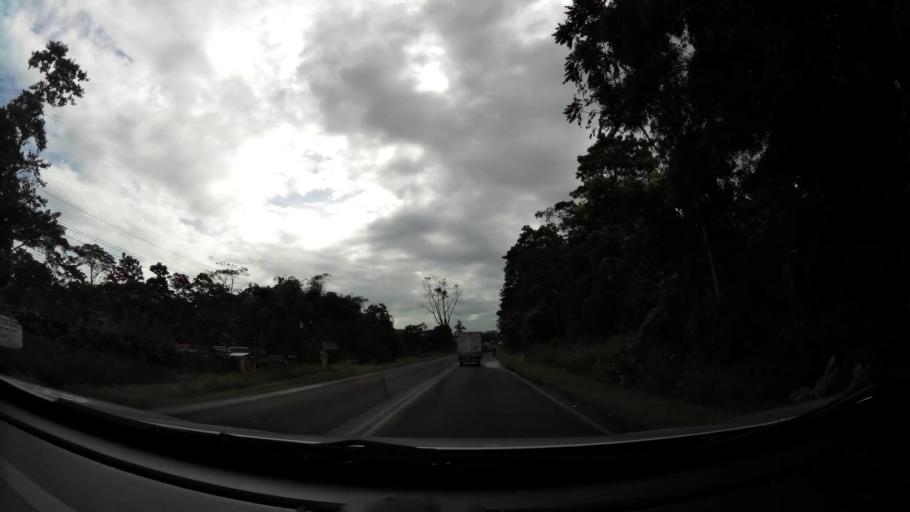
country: CR
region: Limon
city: Pocora
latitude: 10.1724
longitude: -83.6103
